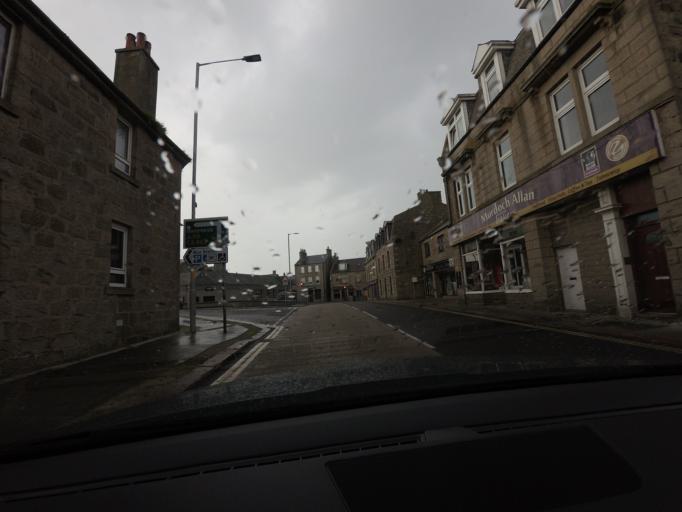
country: GB
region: Scotland
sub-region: Aberdeenshire
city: Fraserburgh
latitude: 57.6933
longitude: -2.0072
